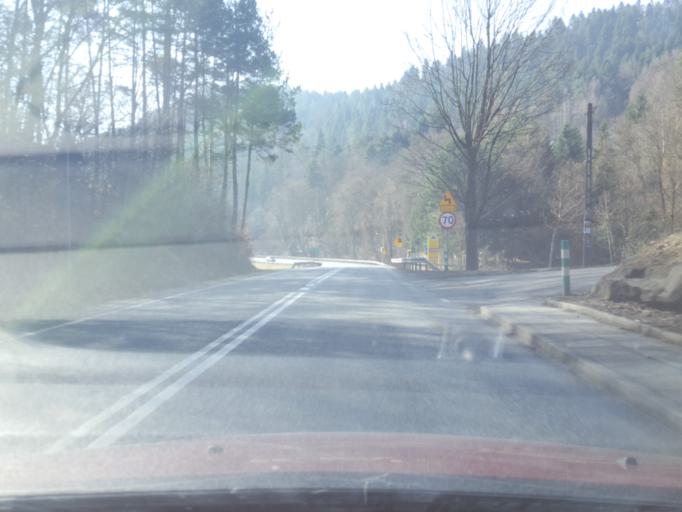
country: PL
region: Lesser Poland Voivodeship
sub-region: Powiat nowosadecki
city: Lososina Dolna
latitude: 49.7968
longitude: 20.6445
